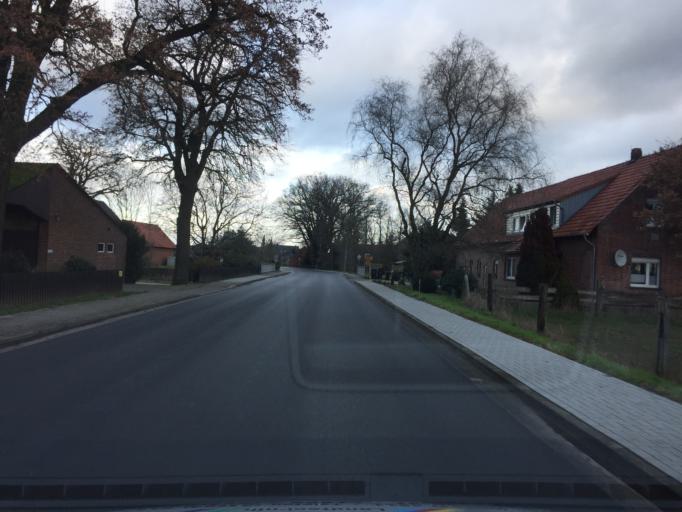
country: DE
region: Lower Saxony
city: Raddestorf
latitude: 52.5067
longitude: 8.9935
